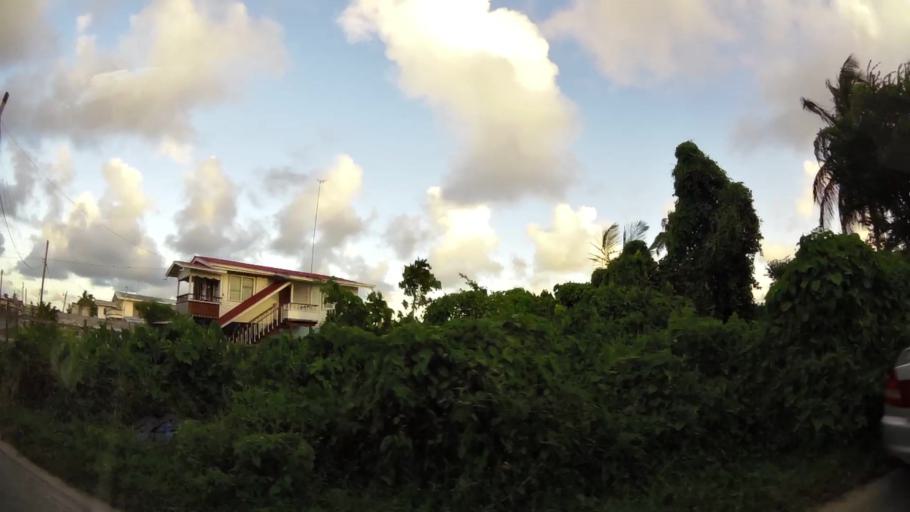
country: GY
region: Demerara-Mahaica
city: Georgetown
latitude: 6.8156
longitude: -58.1096
